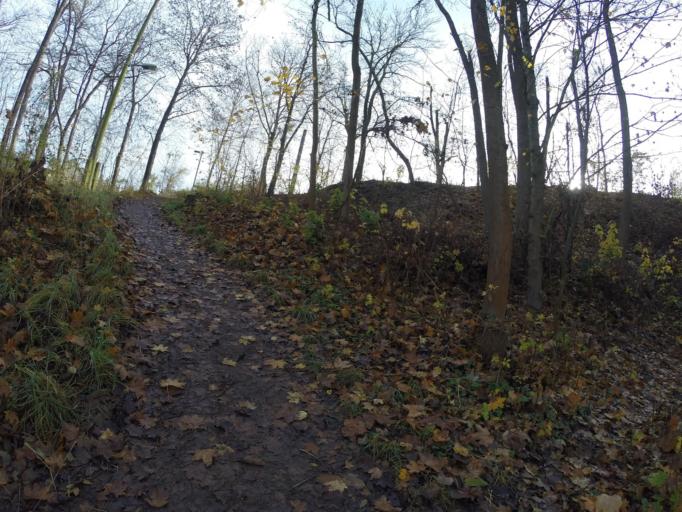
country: DE
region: Thuringia
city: Jena
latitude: 50.9263
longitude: 11.5660
